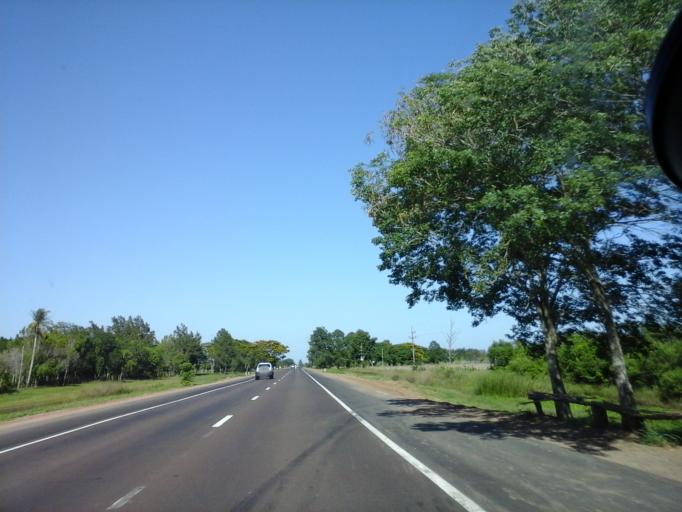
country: AR
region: Corrientes
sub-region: Departamento de Itati
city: Itati
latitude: -27.3667
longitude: -58.3408
